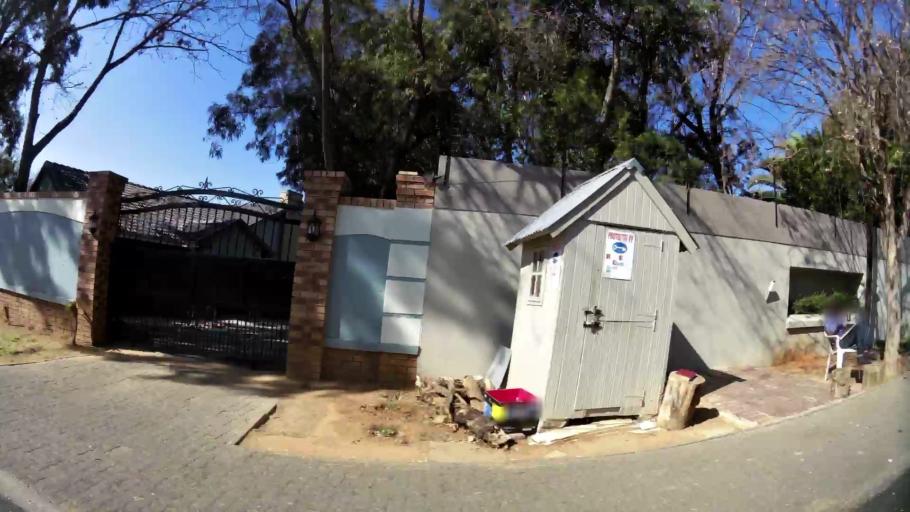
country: ZA
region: Gauteng
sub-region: City of Johannesburg Metropolitan Municipality
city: Modderfontein
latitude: -26.1384
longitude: 28.1114
